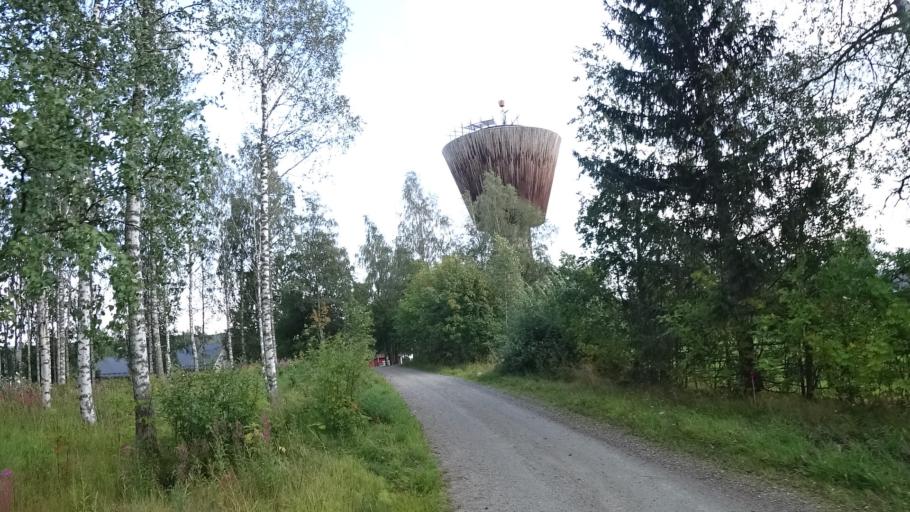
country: FI
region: North Karelia
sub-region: Joensuu
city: Ilomantsi
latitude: 62.6719
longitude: 30.9189
